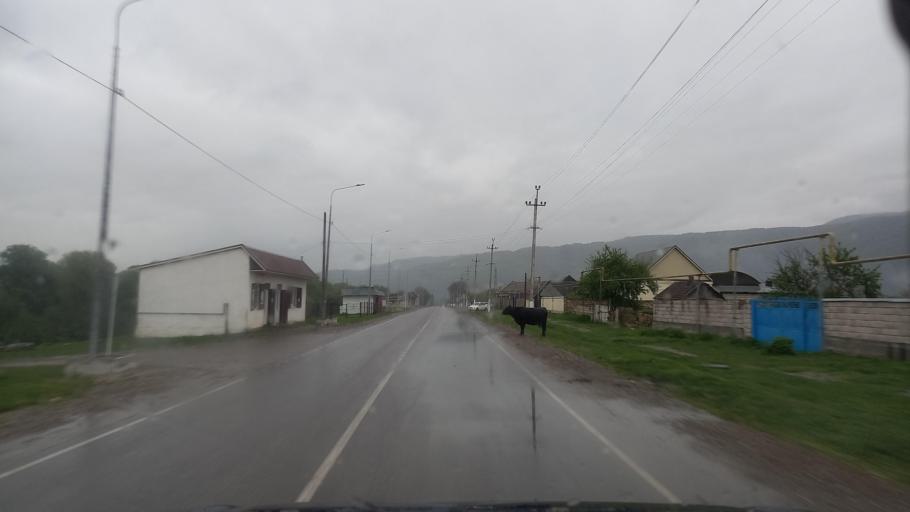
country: RU
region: Kabardino-Balkariya
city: Zhankhoteko
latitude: 43.5887
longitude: 43.2111
